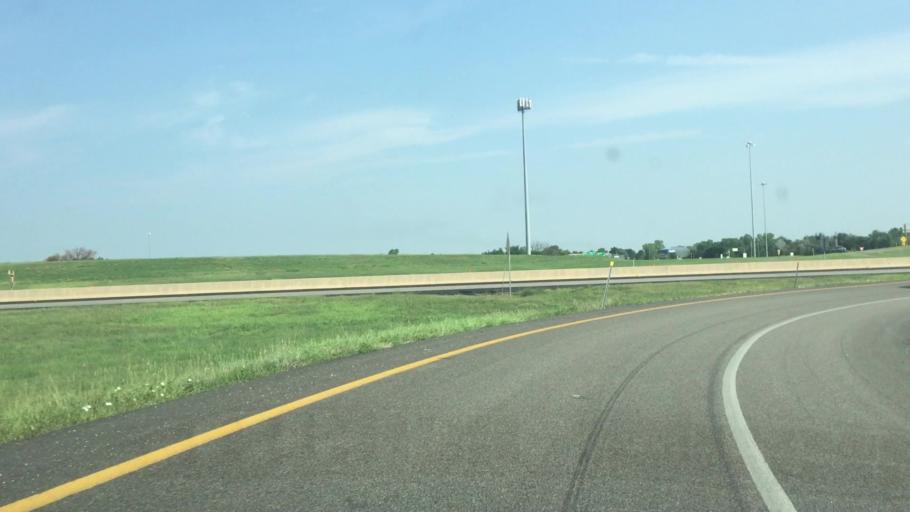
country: US
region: Kansas
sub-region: Butler County
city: Andover
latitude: 37.6856
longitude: -97.1816
